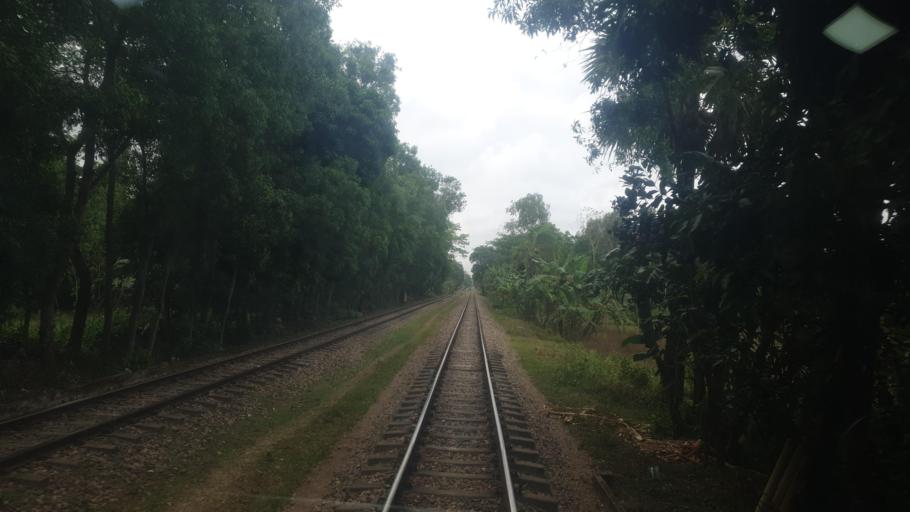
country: BD
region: Chittagong
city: Fatikchari
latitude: 22.6474
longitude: 91.6489
